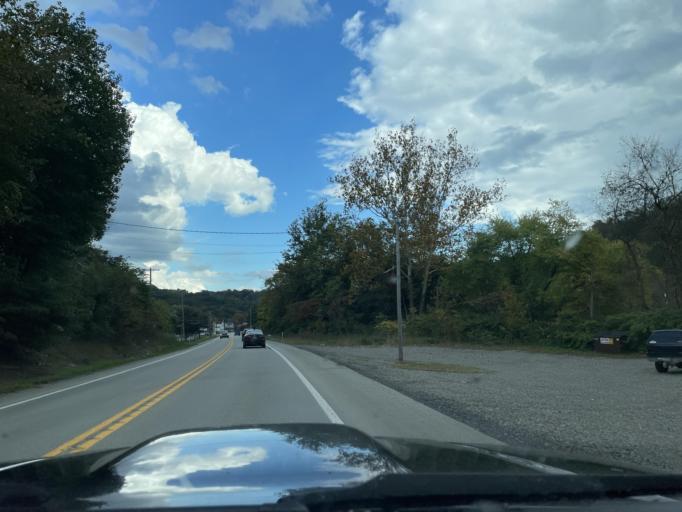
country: US
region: Pennsylvania
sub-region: Westmoreland County
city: Lower Burrell
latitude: 40.5498
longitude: -79.7416
